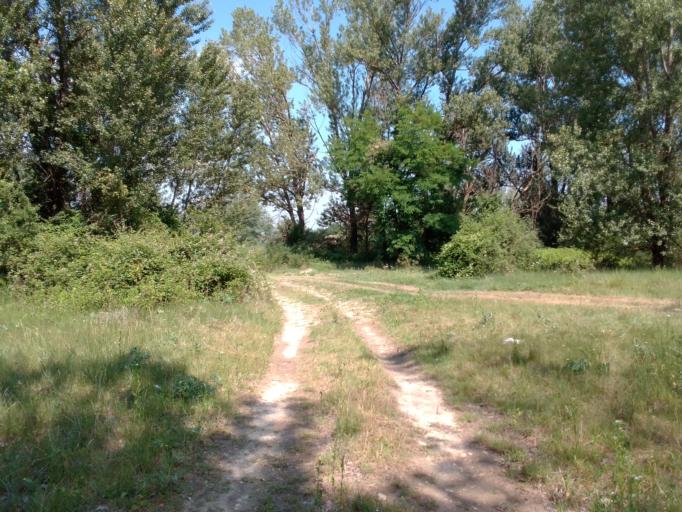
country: IT
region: Emilia-Romagna
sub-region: Provincia di Piacenza
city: Borgonovo Valtidone
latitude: 44.9896
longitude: 9.4775
